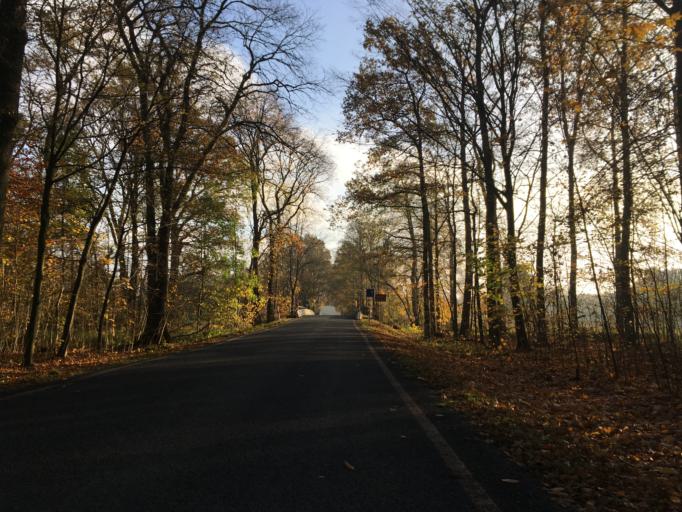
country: DE
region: Brandenburg
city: Schlepzig
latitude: 52.0299
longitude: 13.8740
